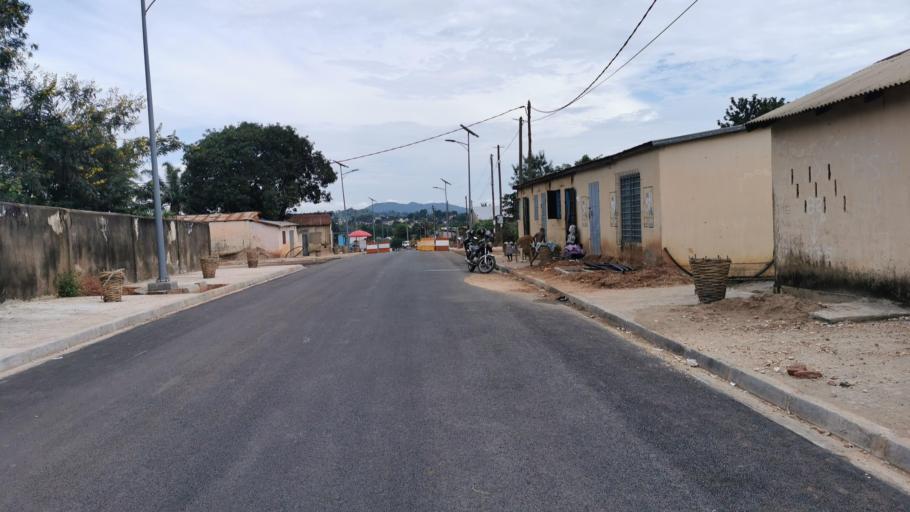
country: TG
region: Kara
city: Kara
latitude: 9.5548
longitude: 1.1927
